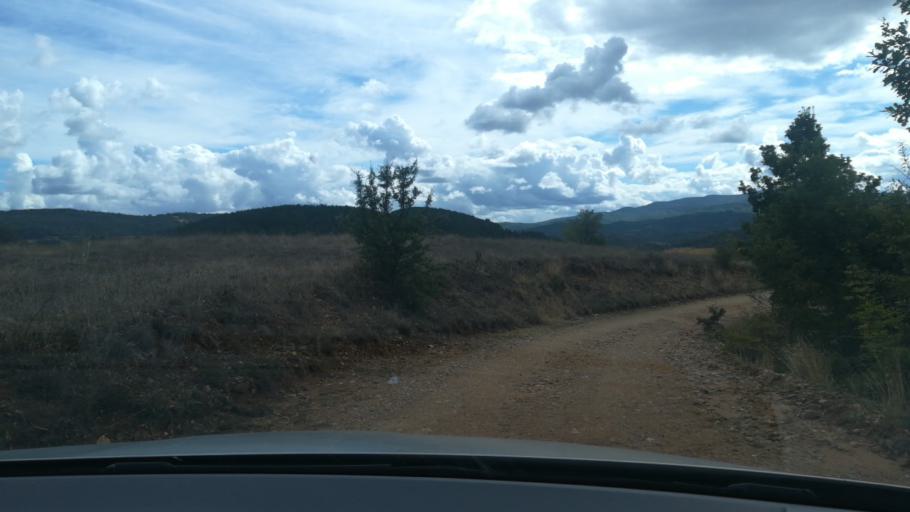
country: MK
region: Makedonska Kamenica
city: Makedonska Kamenica
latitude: 42.0065
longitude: 22.6064
